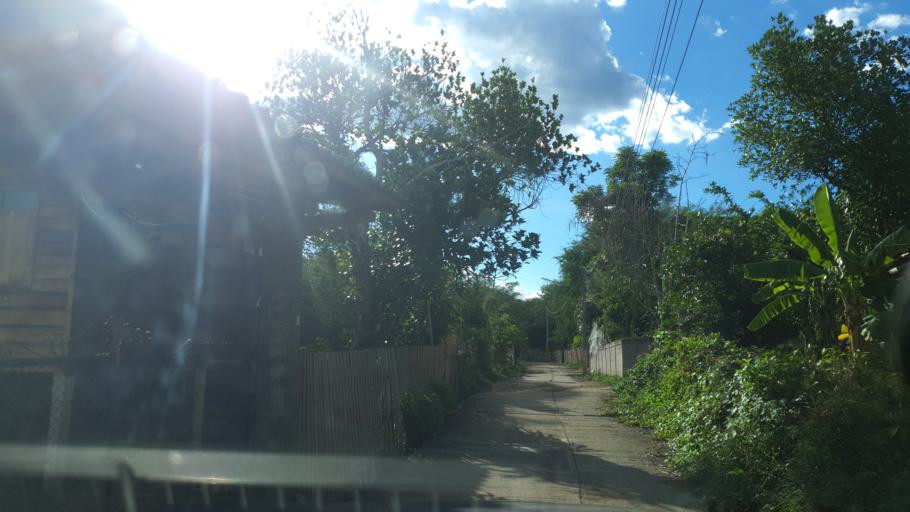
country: TH
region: Lampang
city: Sop Prap
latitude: 17.8803
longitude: 99.2957
